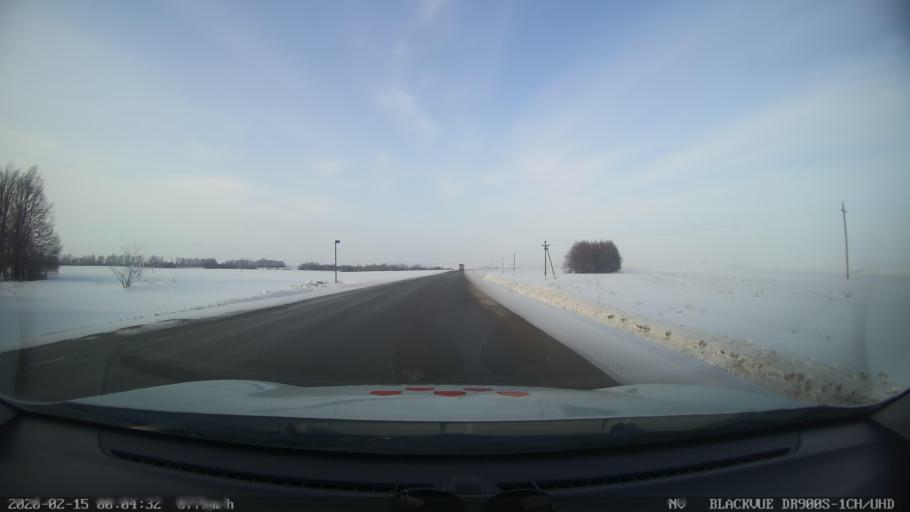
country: RU
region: Tatarstan
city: Kuybyshevskiy Zaton
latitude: 55.3833
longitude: 48.9821
